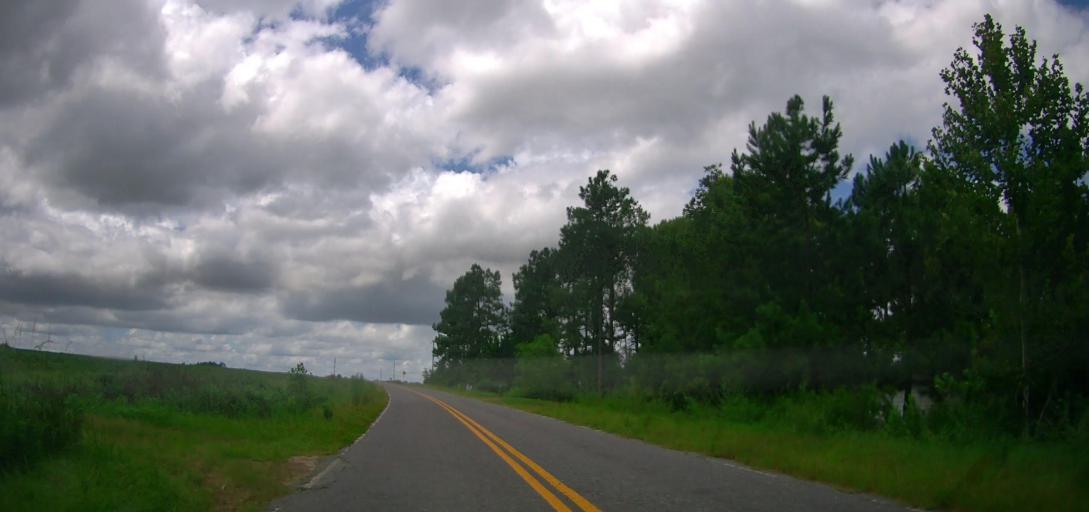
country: US
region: Georgia
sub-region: Irwin County
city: Ocilla
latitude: 31.6475
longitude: -83.3978
